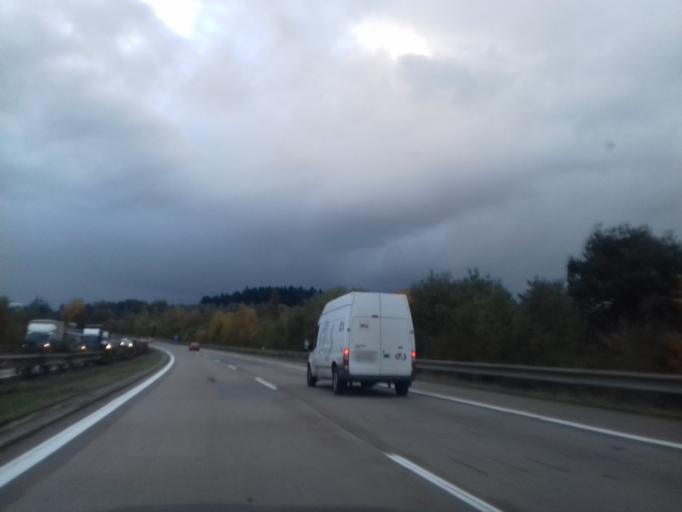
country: CZ
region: Vysocina
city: Heralec
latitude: 49.5162
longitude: 15.4569
